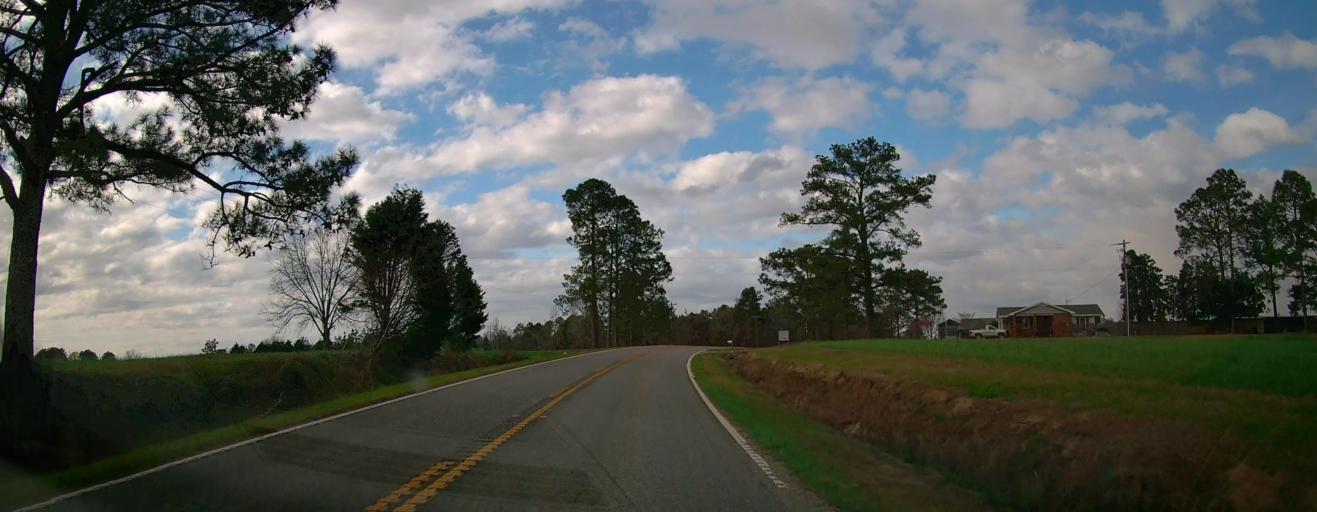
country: US
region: Georgia
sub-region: Marion County
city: Buena Vista
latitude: 32.4429
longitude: -84.4393
